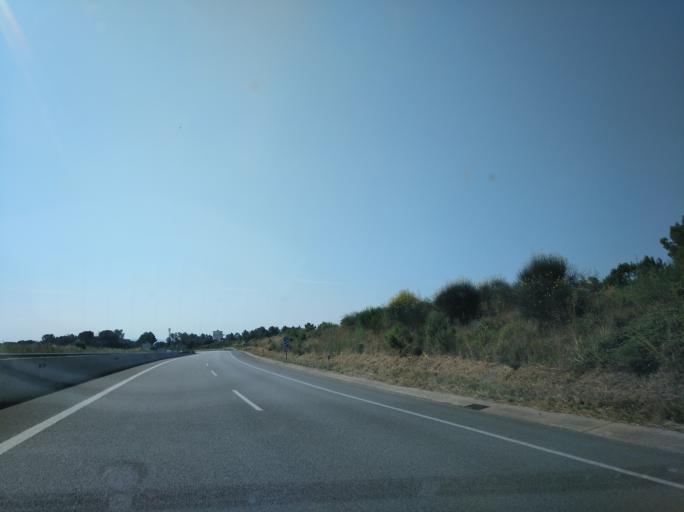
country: ES
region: Catalonia
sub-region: Provincia de Girona
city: Brunyola
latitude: 41.8816
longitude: 2.6874
